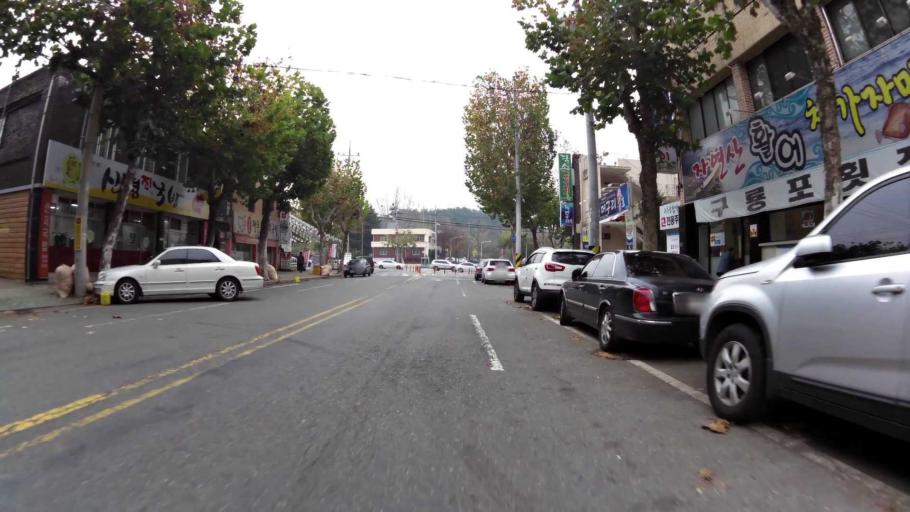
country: KR
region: Daegu
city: Daegu
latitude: 35.8601
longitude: 128.6459
